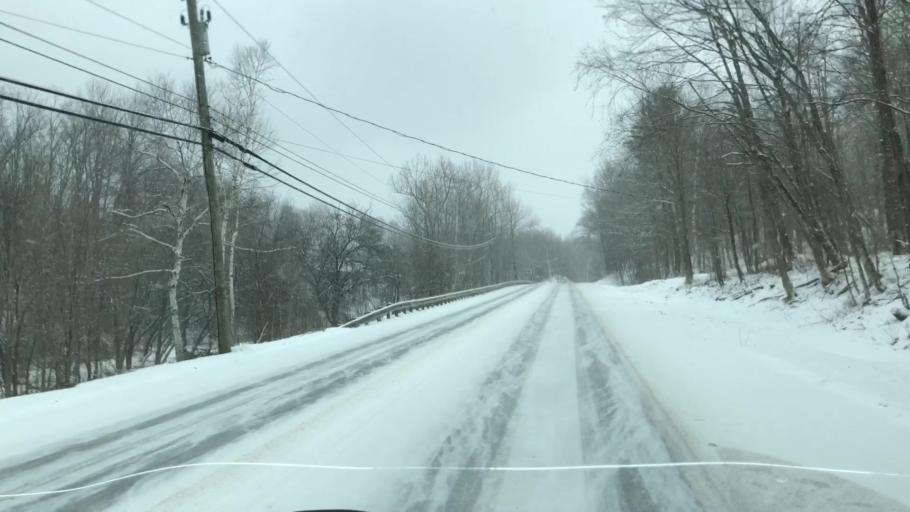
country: US
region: Massachusetts
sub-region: Berkshire County
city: Adams
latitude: 42.5815
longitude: -73.0650
